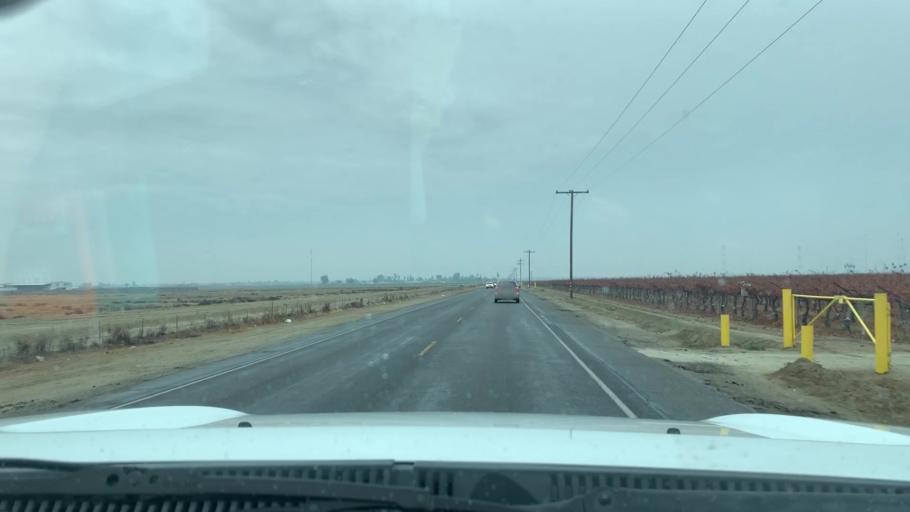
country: US
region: California
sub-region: Kern County
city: Delano
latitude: 35.7613
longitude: -119.3097
